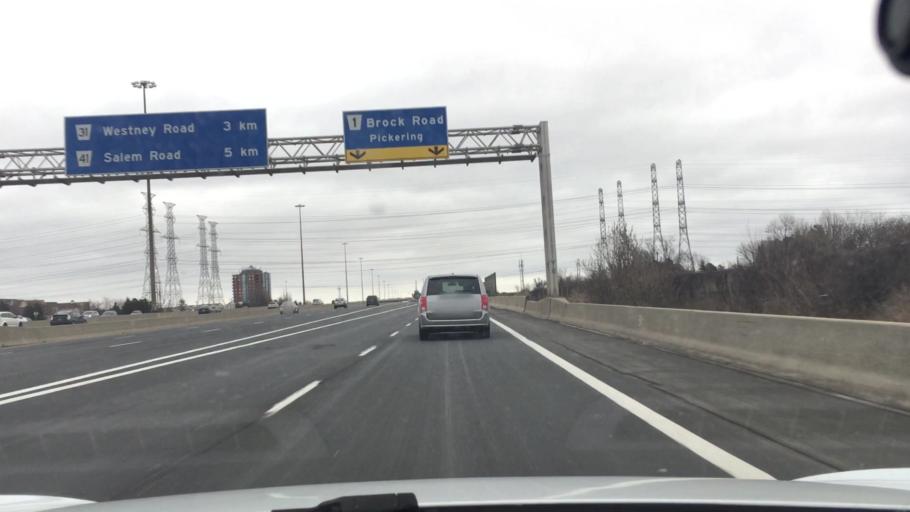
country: CA
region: Ontario
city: Ajax
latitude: 43.8345
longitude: -79.0793
